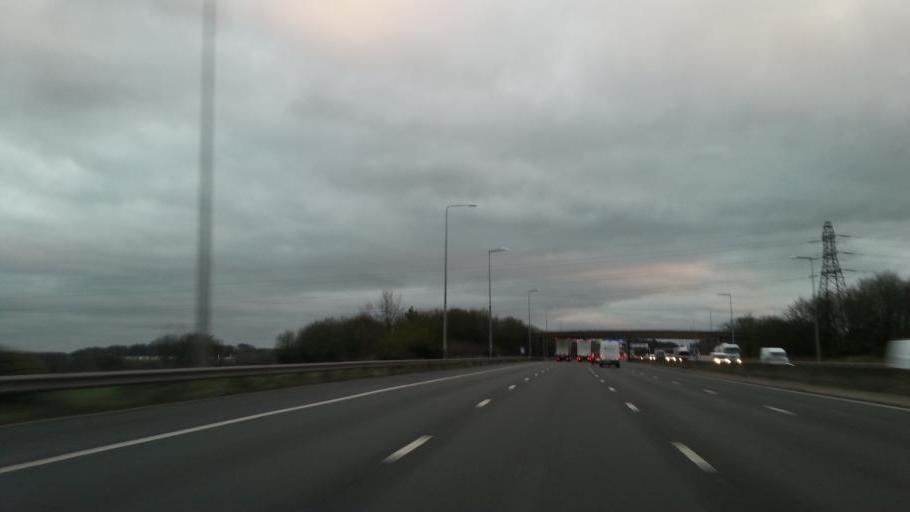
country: GB
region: England
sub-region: Derbyshire
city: Pinxton
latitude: 53.0704
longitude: -1.2783
